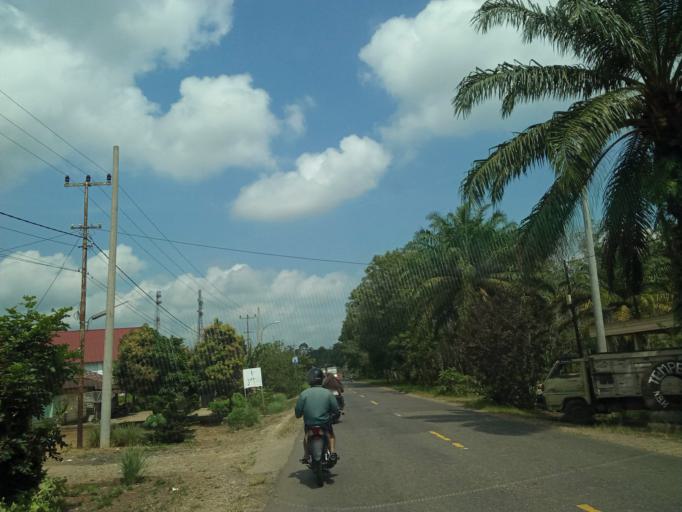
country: ID
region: Jambi
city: Muara Tembesi
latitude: -1.7177
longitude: 103.1253
